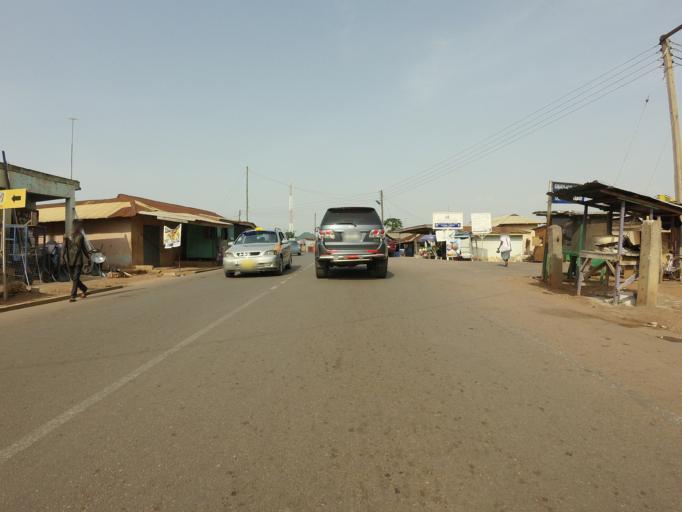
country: GH
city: Akropong
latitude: 6.1021
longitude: -0.0159
